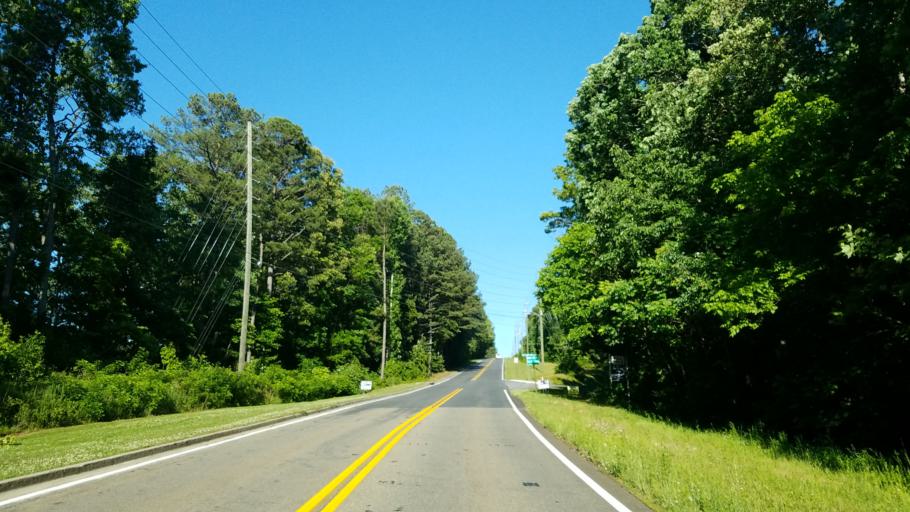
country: US
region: Georgia
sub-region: Cherokee County
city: Holly Springs
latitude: 34.1751
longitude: -84.5171
